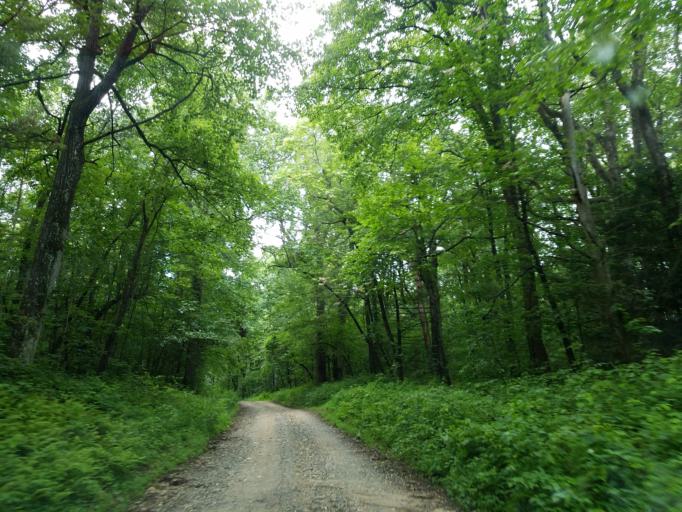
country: US
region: Georgia
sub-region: Lumpkin County
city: Dahlonega
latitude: 34.6412
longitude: -84.1602
